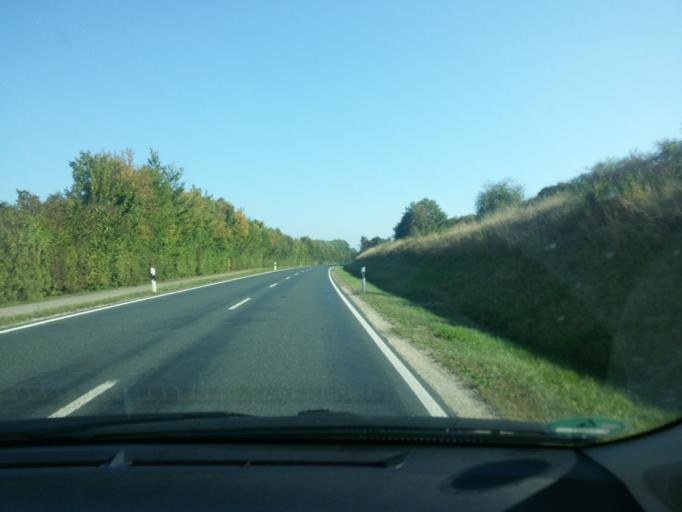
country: DE
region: Bavaria
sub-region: Swabia
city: Hainsfarth
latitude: 48.9715
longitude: 10.6191
